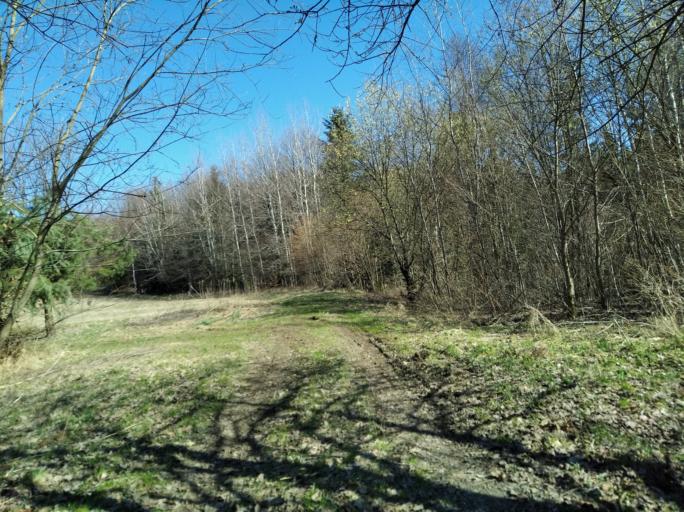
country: PL
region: Subcarpathian Voivodeship
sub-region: Powiat strzyzowski
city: Jawornik
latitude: 49.8349
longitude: 21.8511
